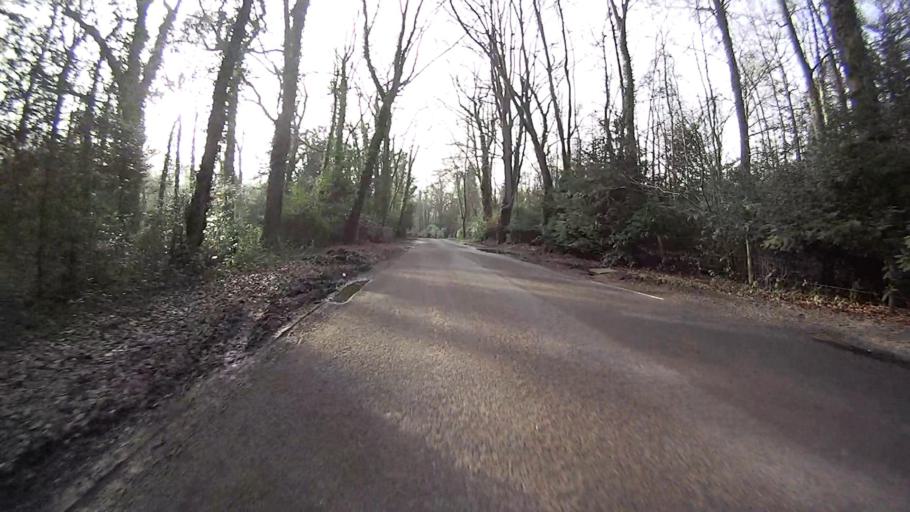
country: GB
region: England
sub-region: West Sussex
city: Crawley Down
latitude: 51.1173
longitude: -0.0946
